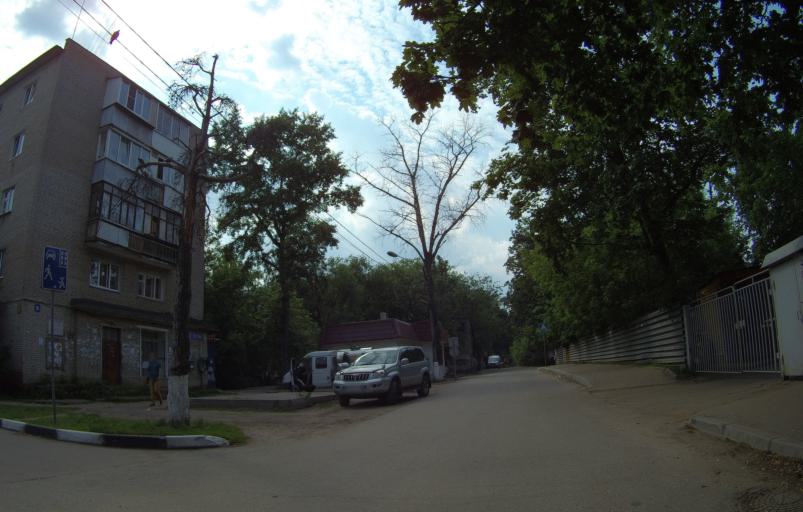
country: RU
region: Moskovskaya
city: Vereya
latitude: 55.6308
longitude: 38.0481
